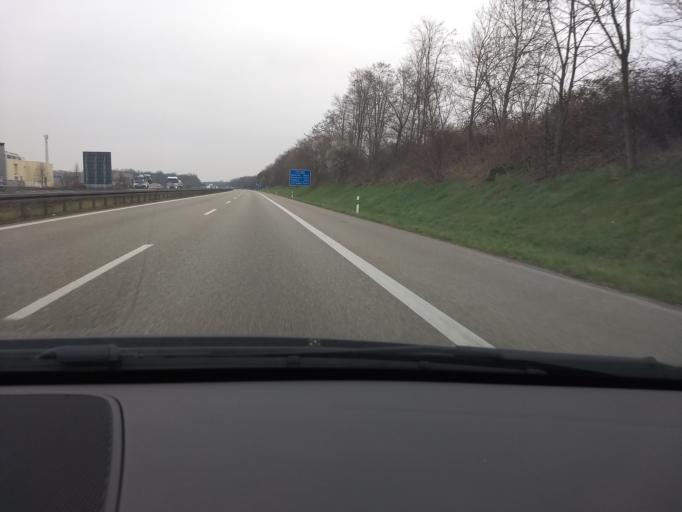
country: DE
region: Baden-Wuerttemberg
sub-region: Freiburg Region
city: Neuenburg am Rhein
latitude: 47.8204
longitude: 7.5577
